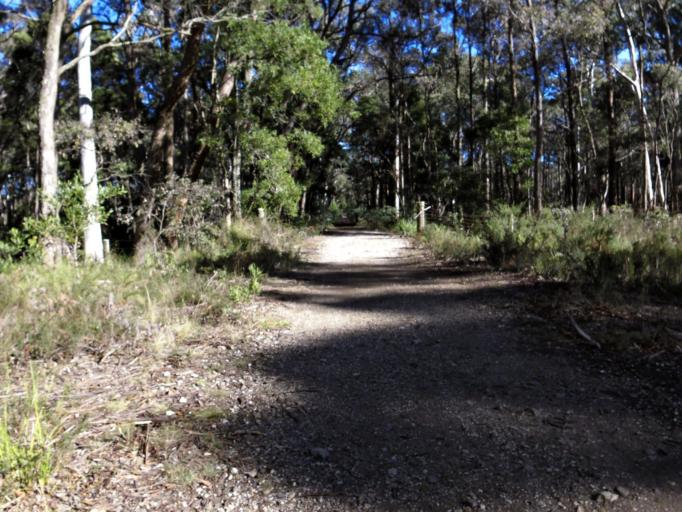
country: AU
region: Victoria
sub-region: Moorabool
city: Bacchus Marsh
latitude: -37.3896
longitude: 144.2963
